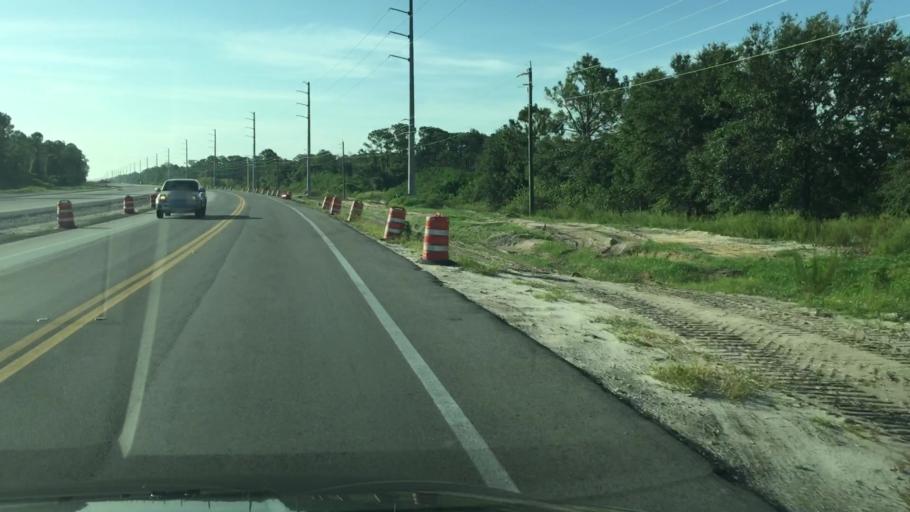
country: US
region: Florida
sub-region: Lee County
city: Gateway
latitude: 26.5923
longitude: -81.7375
